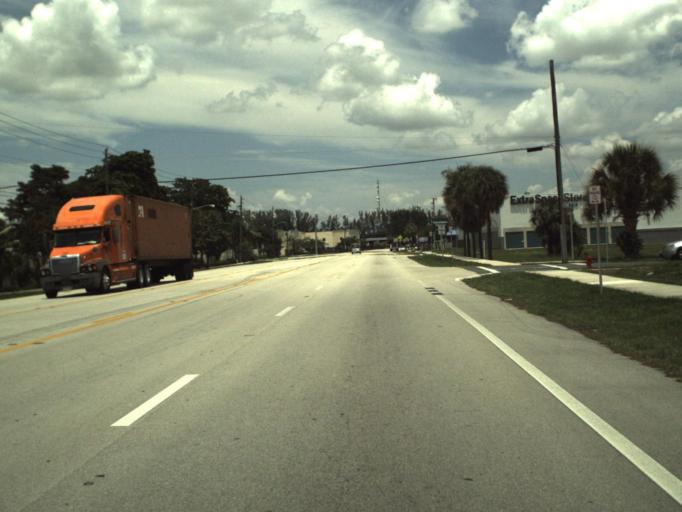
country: US
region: Florida
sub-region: Broward County
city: Coconut Creek
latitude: 26.2377
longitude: -80.1656
